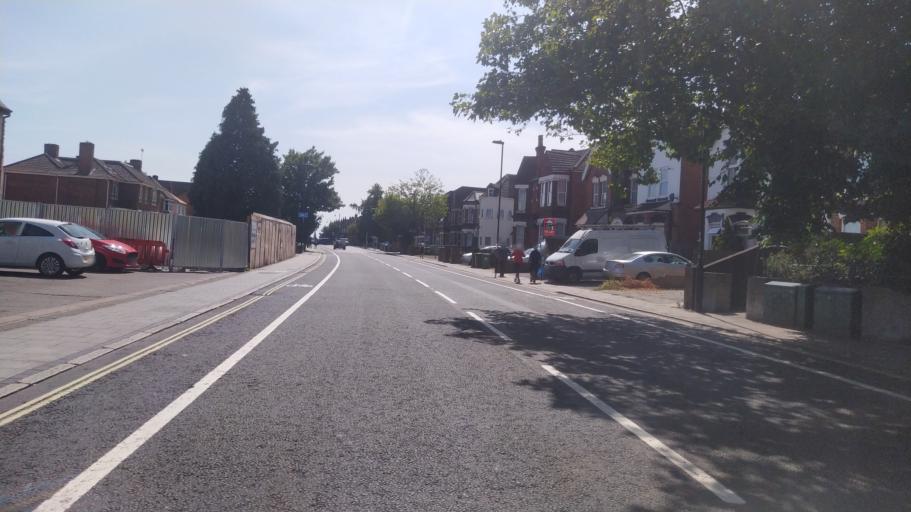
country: GB
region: England
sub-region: Southampton
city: Southampton
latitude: 50.9228
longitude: -1.3954
